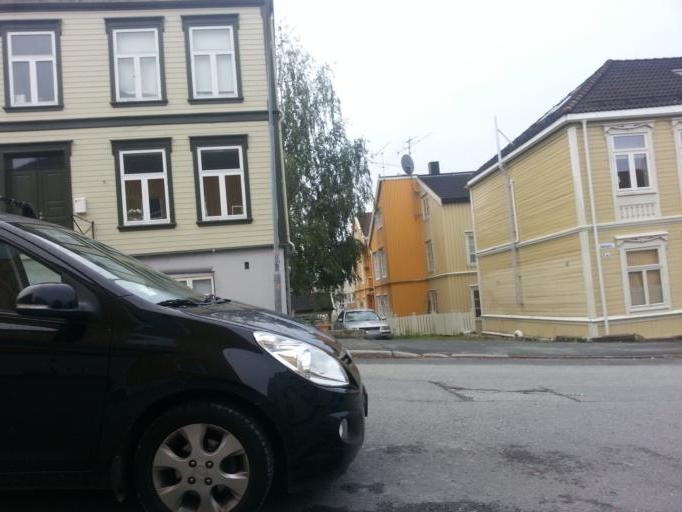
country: NO
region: Sor-Trondelag
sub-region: Trondheim
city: Trondheim
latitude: 63.4314
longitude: 10.4099
